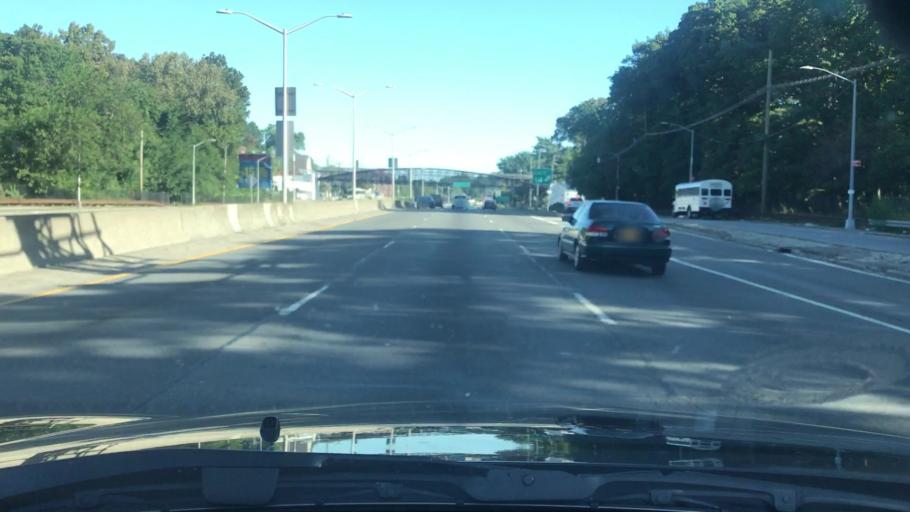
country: US
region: New York
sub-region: Westchester County
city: Yonkers
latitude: 40.9044
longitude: -73.8783
